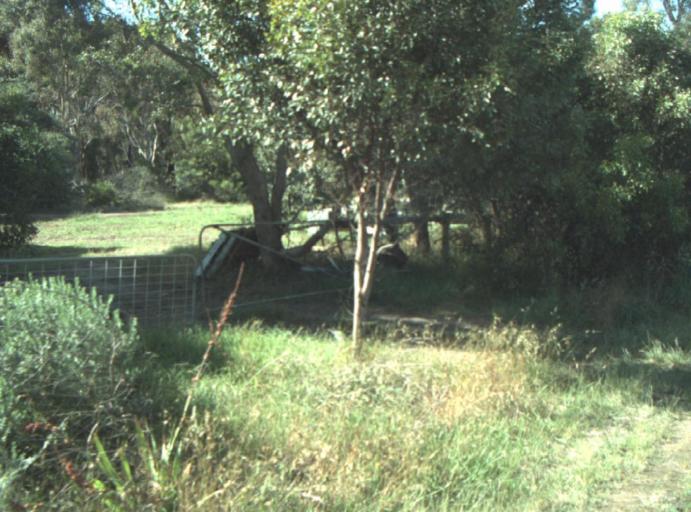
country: AU
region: Victoria
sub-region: Greater Geelong
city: Clifton Springs
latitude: -38.2370
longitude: 144.5769
